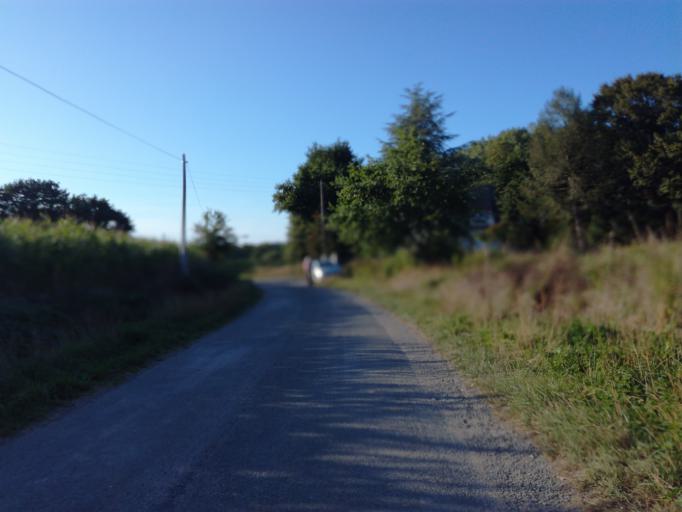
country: FR
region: Brittany
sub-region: Departement d'Ille-et-Vilaine
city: Betton
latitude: 48.1683
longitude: -1.6360
